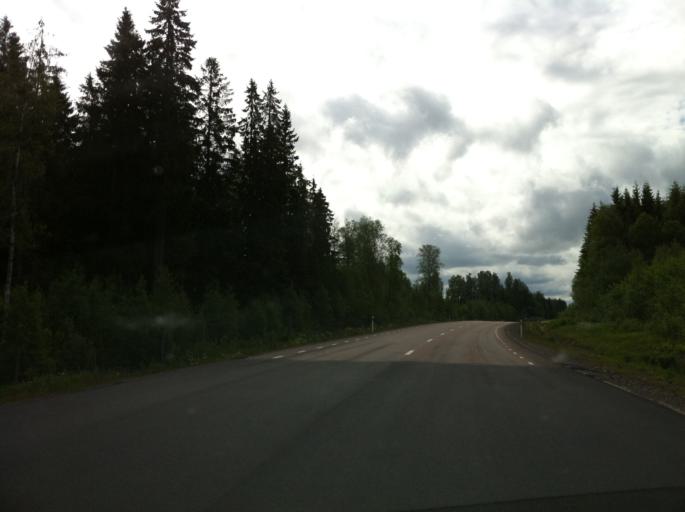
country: SE
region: Vaermland
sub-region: Sunne Kommun
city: Sunne
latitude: 59.7448
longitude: 13.1265
